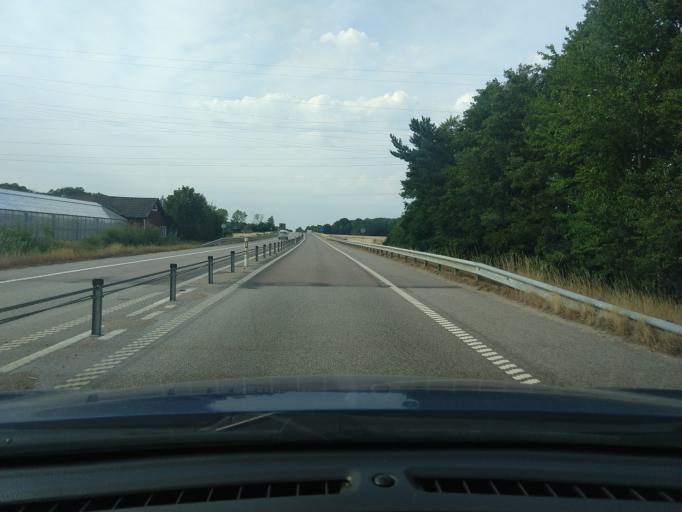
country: SE
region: Blekinge
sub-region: Ronneby Kommun
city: Kallinge
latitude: 56.2339
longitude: 15.2591
